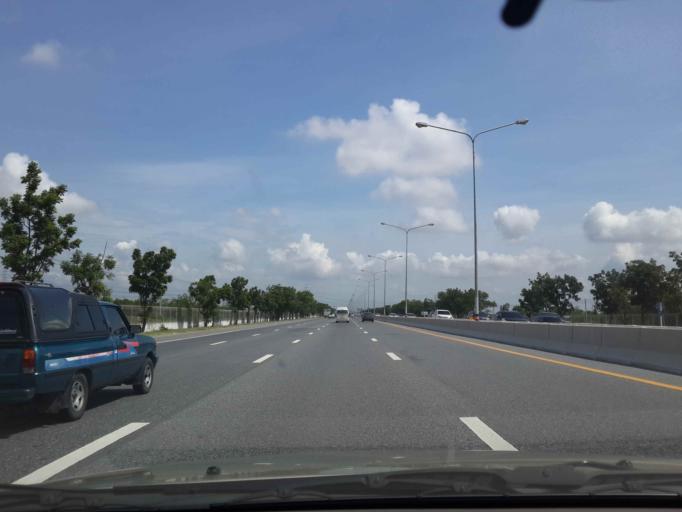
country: TH
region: Chachoengsao
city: Bang Pakong
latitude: 13.5138
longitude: 101.0303
